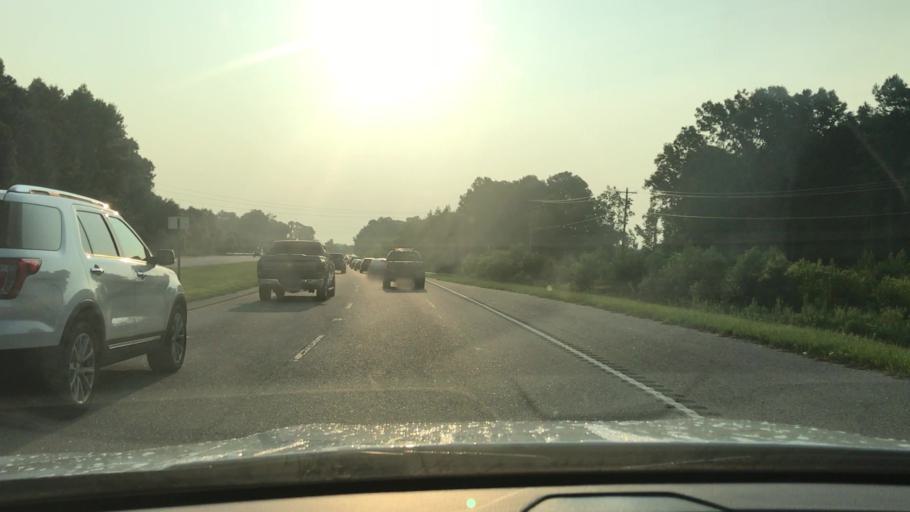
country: US
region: South Carolina
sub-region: Charleston County
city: Shell Point
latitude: 32.8110
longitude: -80.0535
